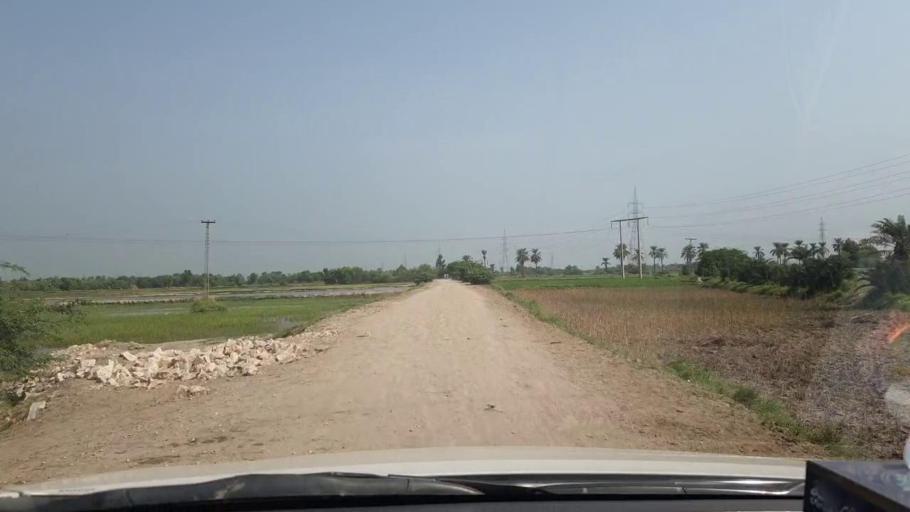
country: PK
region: Sindh
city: Shikarpur
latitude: 27.9707
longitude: 68.6654
